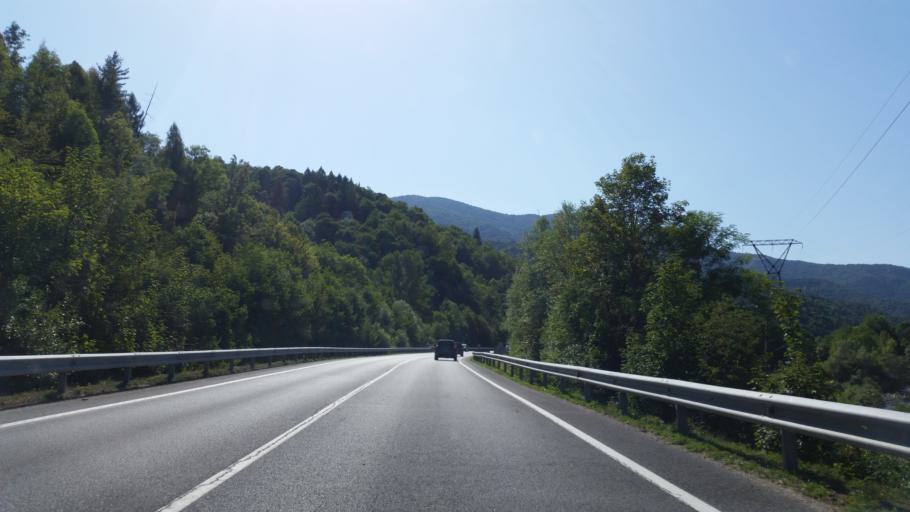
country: IT
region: Piedmont
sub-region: Provincia di Cuneo
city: Robilante
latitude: 44.3037
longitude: 7.5124
